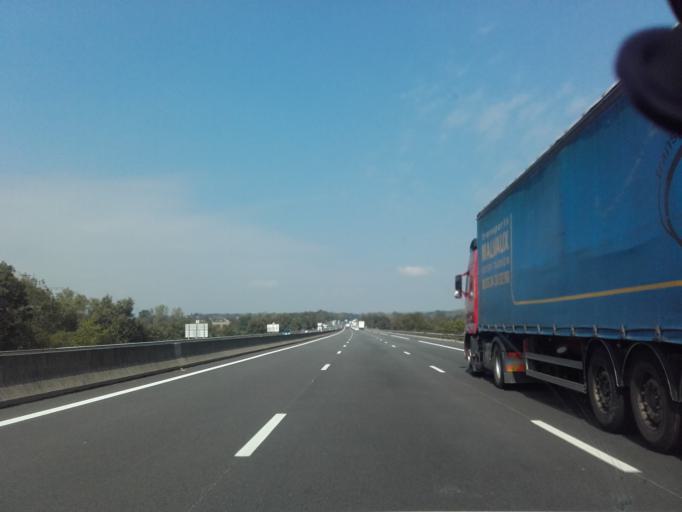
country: FR
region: Bourgogne
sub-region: Departement de Saone-et-Loire
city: Saint-Martin-Belle-Roche
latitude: 46.4316
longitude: 4.8694
